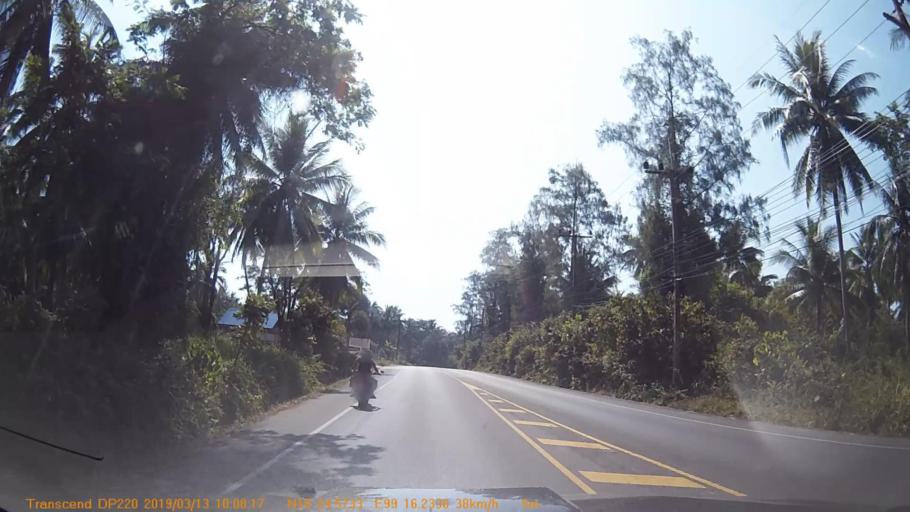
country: TH
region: Chumphon
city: Chumphon
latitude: 10.4095
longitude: 99.2707
